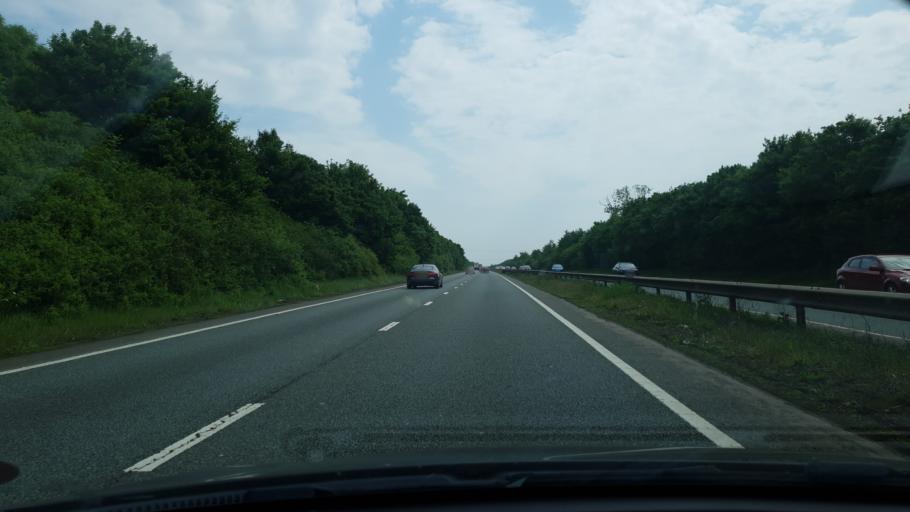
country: GB
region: England
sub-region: Northamptonshire
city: Desborough
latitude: 52.4052
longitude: -0.8781
